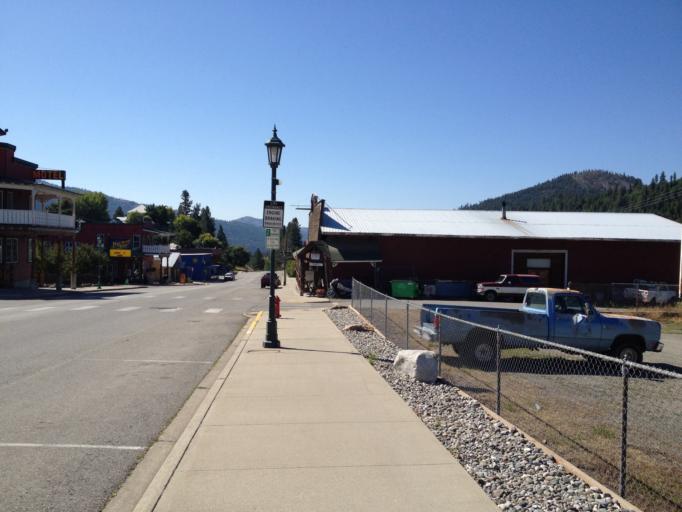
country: US
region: Washington
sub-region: Ferry County
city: Republic
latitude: 48.6461
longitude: -118.7379
